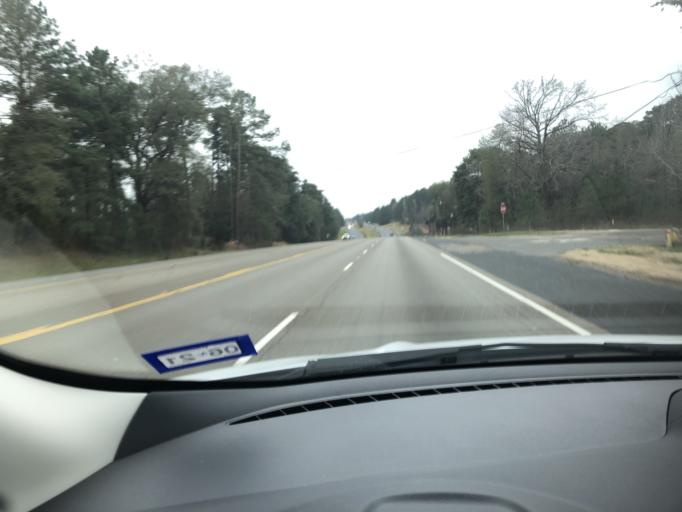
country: US
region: Texas
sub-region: Nacogdoches County
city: Nacogdoches
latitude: 31.5505
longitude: -94.6868
